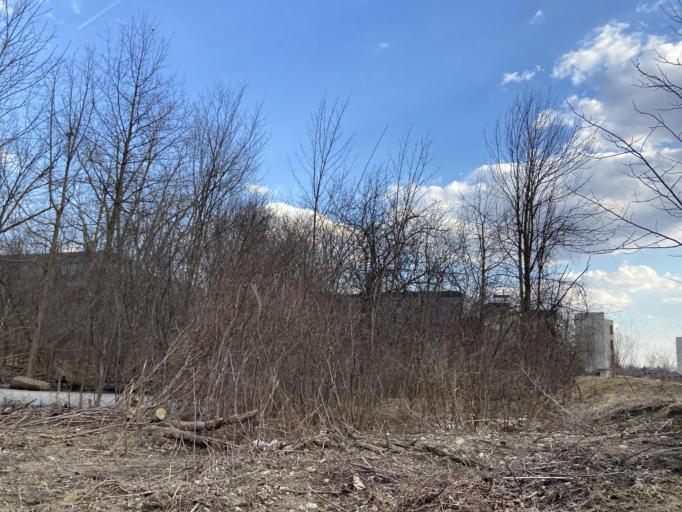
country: US
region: Michigan
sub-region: Oakland County
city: Southfield
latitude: 42.4830
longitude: -83.2523
